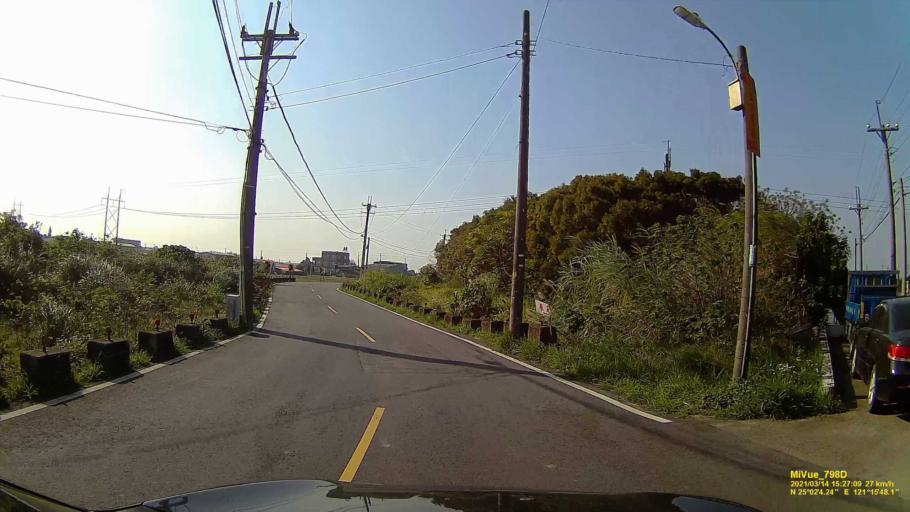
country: TW
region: Taiwan
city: Taoyuan City
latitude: 25.0346
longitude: 121.2633
